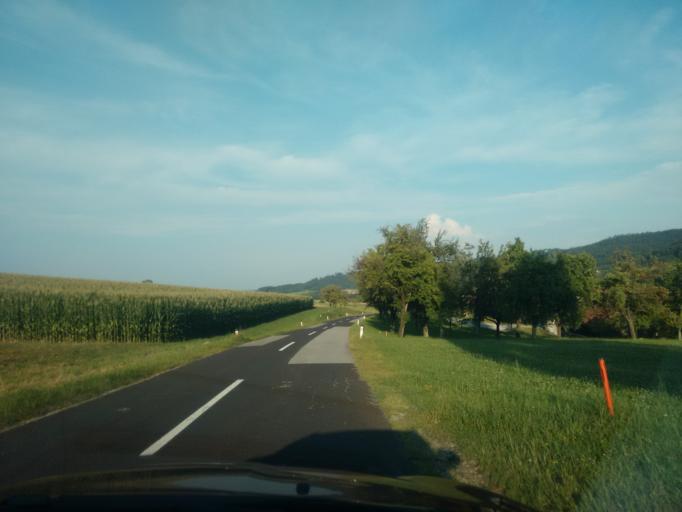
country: AT
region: Upper Austria
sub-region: Politischer Bezirk Vocklabruck
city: Wolfsegg am Hausruck
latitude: 48.1494
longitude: 13.6197
